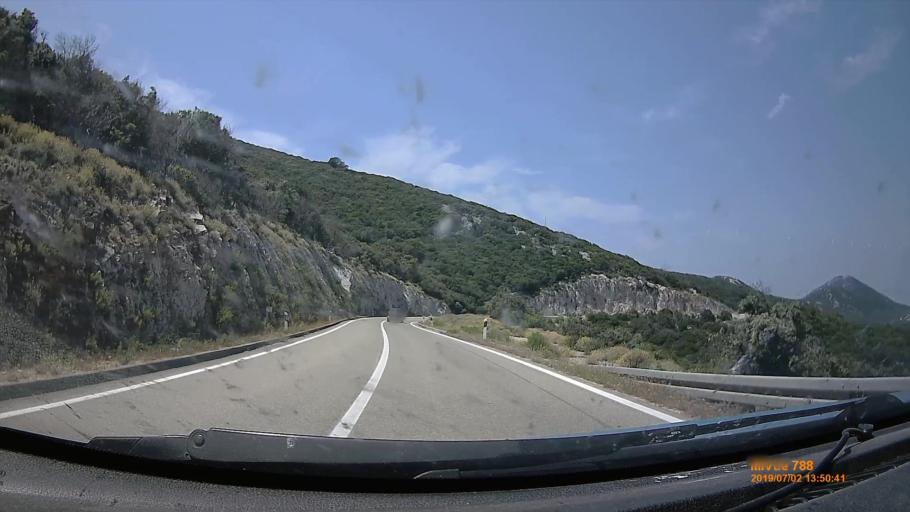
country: HR
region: Primorsko-Goranska
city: Mali Losinj
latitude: 44.5988
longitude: 14.4086
